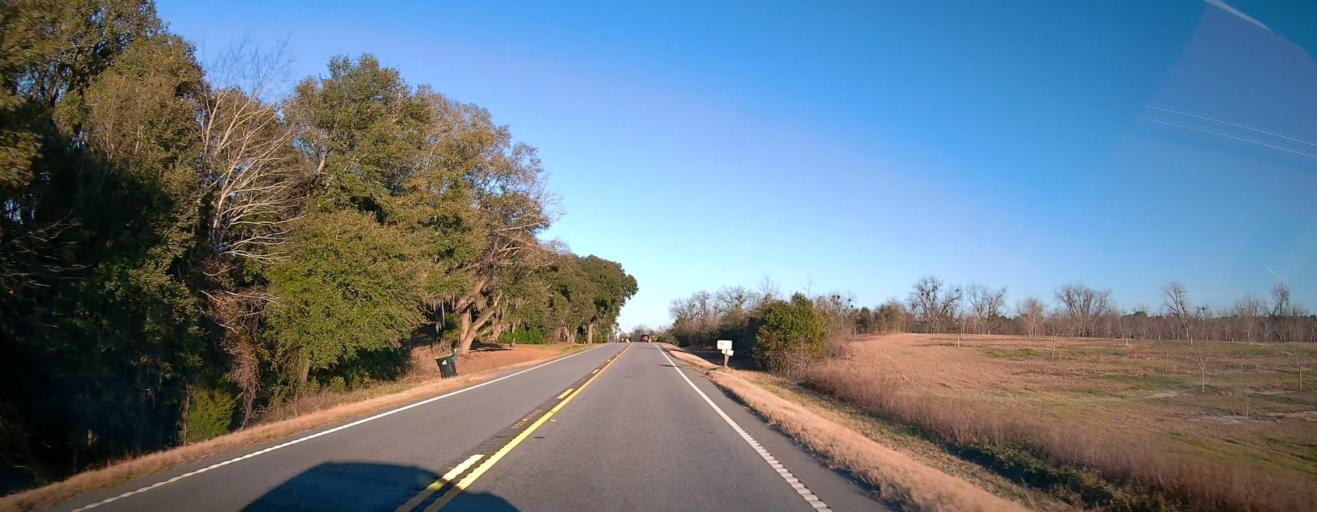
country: US
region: Georgia
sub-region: Dougherty County
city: Albany
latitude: 31.5041
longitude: -84.2173
